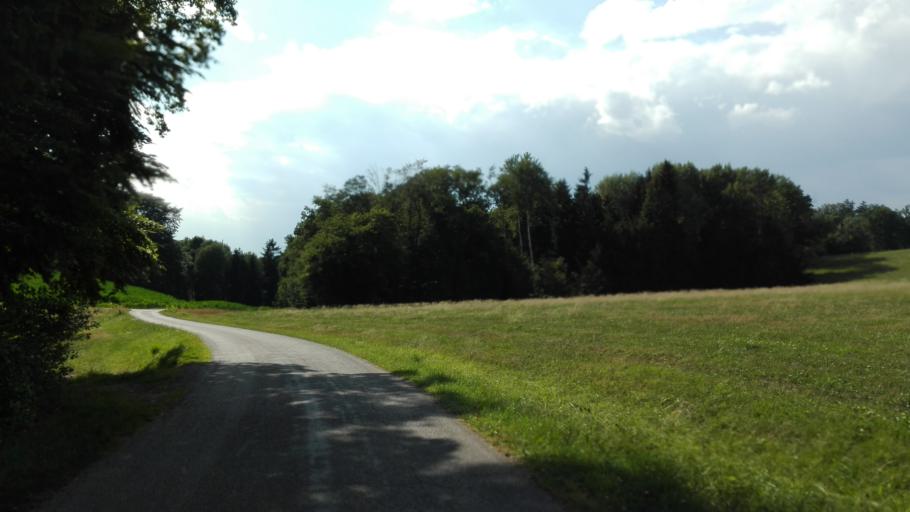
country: AT
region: Upper Austria
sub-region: Politischer Bezirk Perg
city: Bad Kreuzen
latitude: 48.2450
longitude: 14.7287
